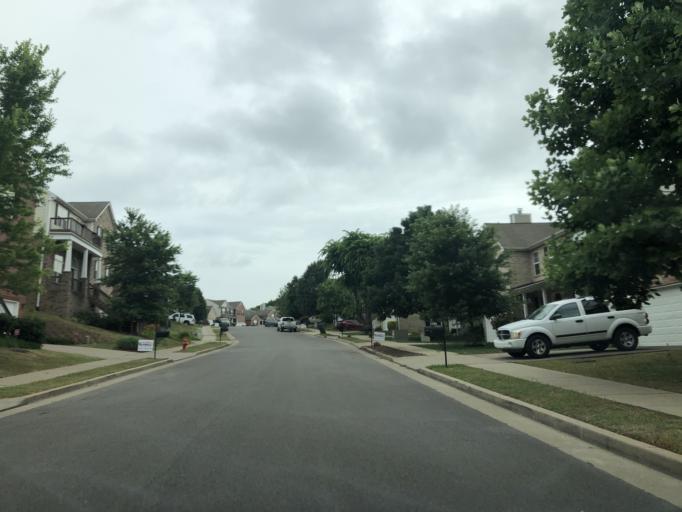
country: US
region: Tennessee
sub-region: Davidson County
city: Goodlettsville
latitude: 36.2707
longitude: -86.7742
